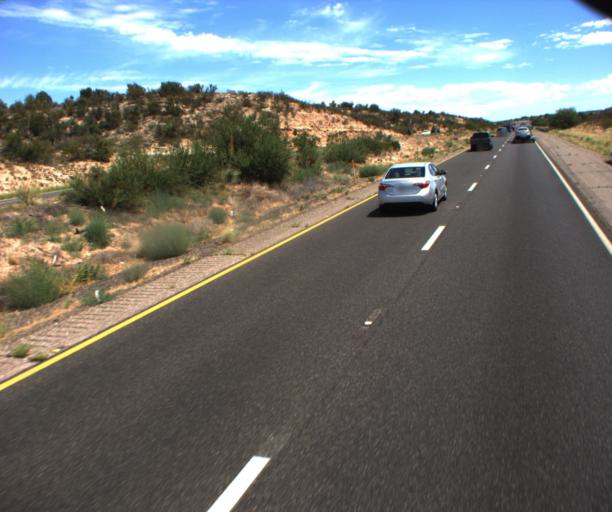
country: US
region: Arizona
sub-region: Yavapai County
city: Lake Montezuma
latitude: 34.6472
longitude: -111.8030
